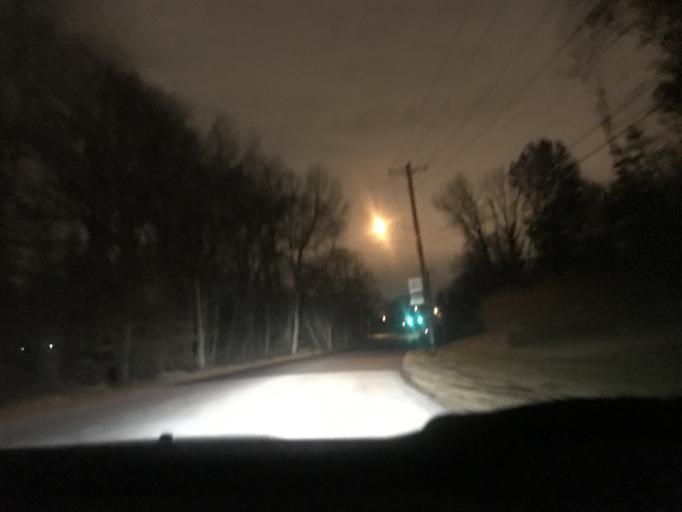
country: US
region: Maryland
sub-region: Prince George's County
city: Oxon Hill
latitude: 38.8036
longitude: -76.9688
